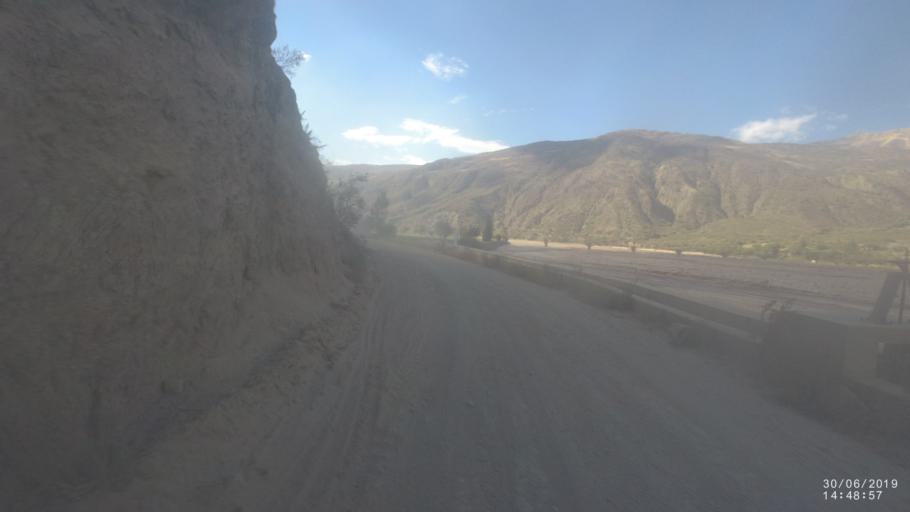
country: BO
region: Cochabamba
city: Irpa Irpa
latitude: -17.7862
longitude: -66.3417
